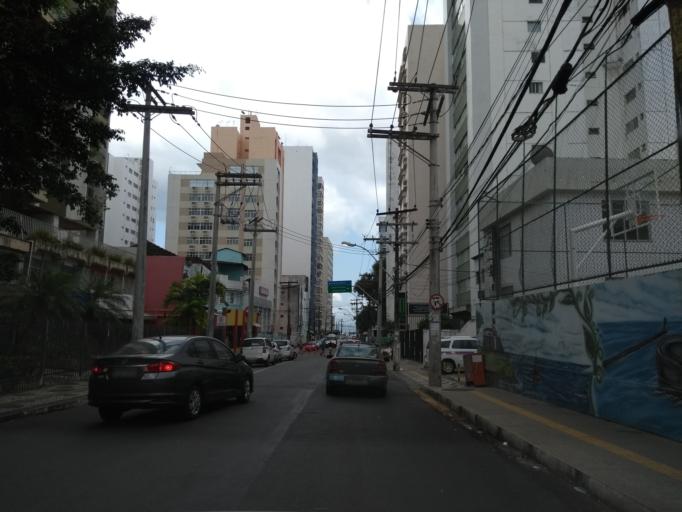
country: BR
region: Bahia
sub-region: Salvador
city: Salvador
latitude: -13.0036
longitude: -38.5299
